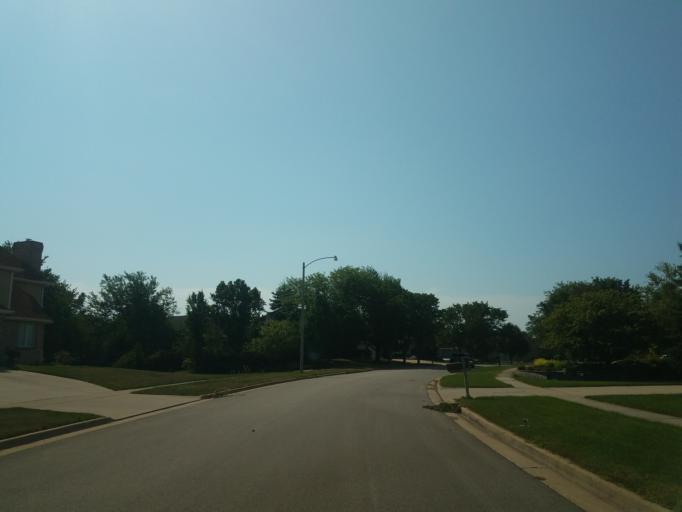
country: US
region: Illinois
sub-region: McLean County
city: Normal
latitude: 40.5042
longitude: -88.9167
